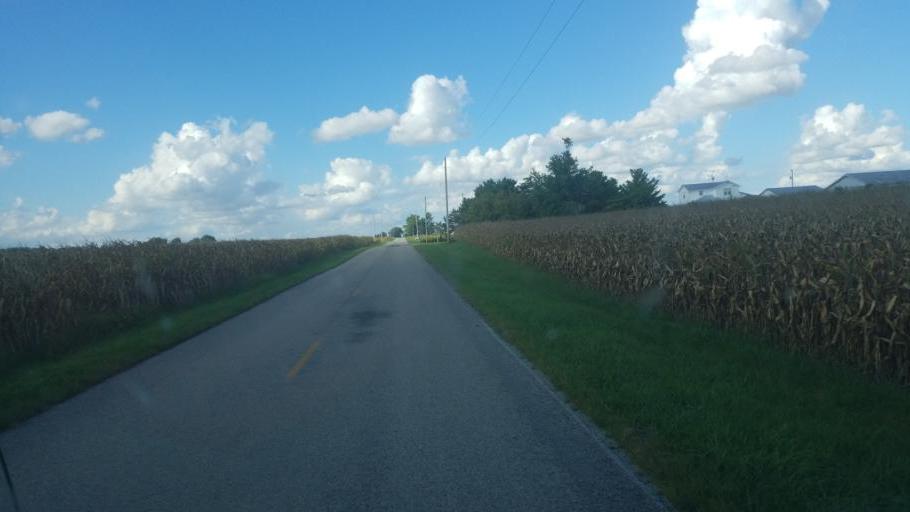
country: US
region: Ohio
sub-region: Hardin County
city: Kenton
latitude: 40.7117
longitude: -83.6918
